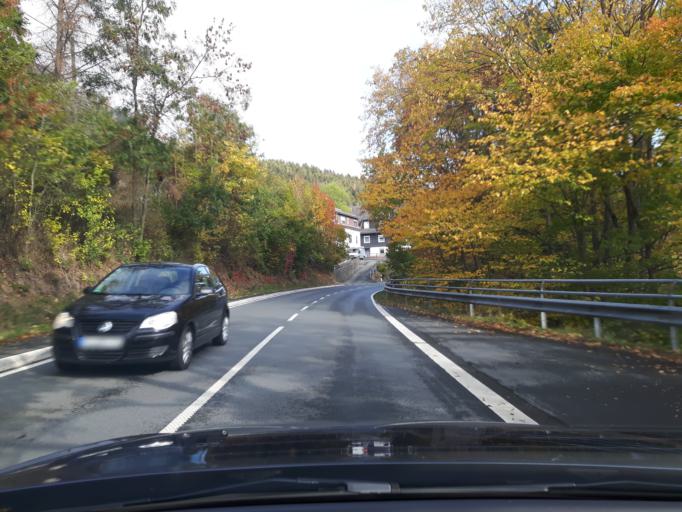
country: DE
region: North Rhine-Westphalia
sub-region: Regierungsbezirk Arnsberg
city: Bad Berleburg
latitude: 51.0235
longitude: 8.4611
